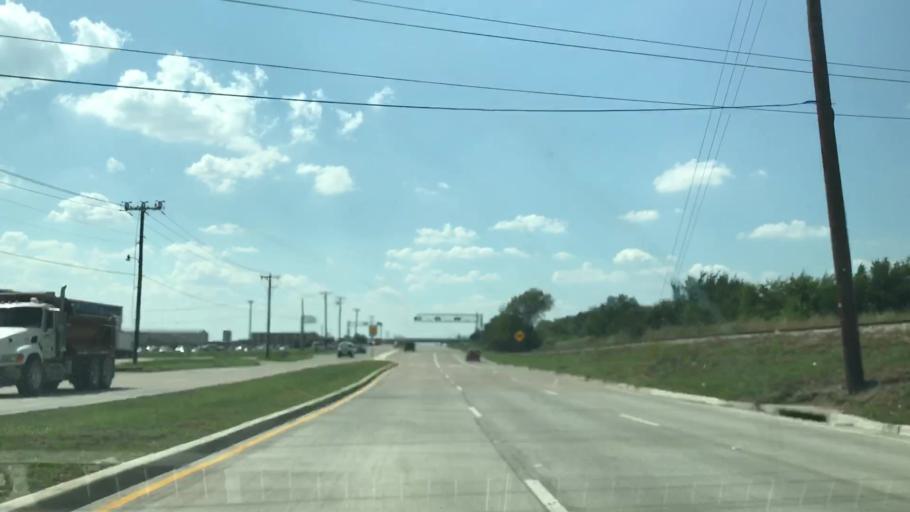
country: US
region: Texas
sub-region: Dallas County
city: Carrollton
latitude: 32.9525
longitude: -96.9142
